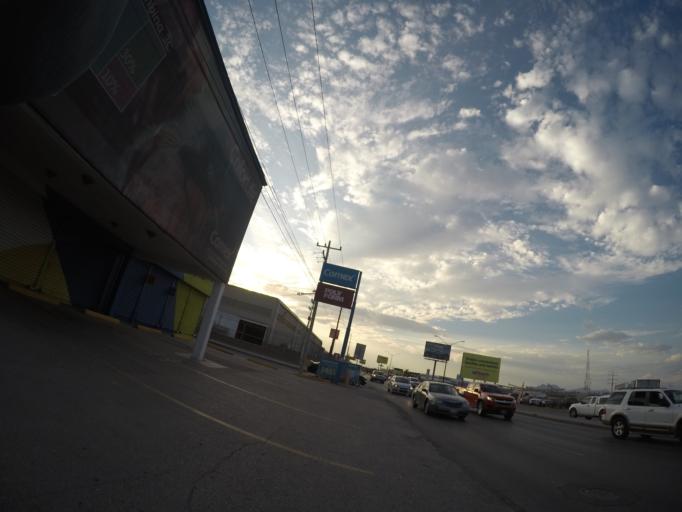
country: MX
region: Chihuahua
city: Ciudad Juarez
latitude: 31.7041
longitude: -106.4208
